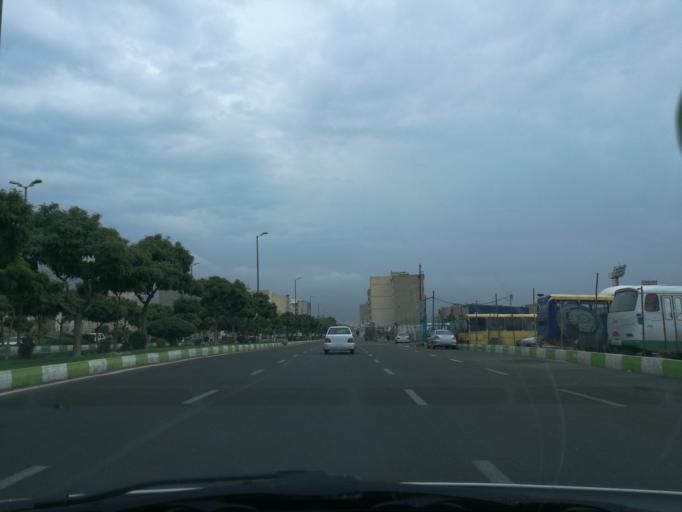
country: IR
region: Alborz
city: Karaj
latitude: 35.8537
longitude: 50.9594
